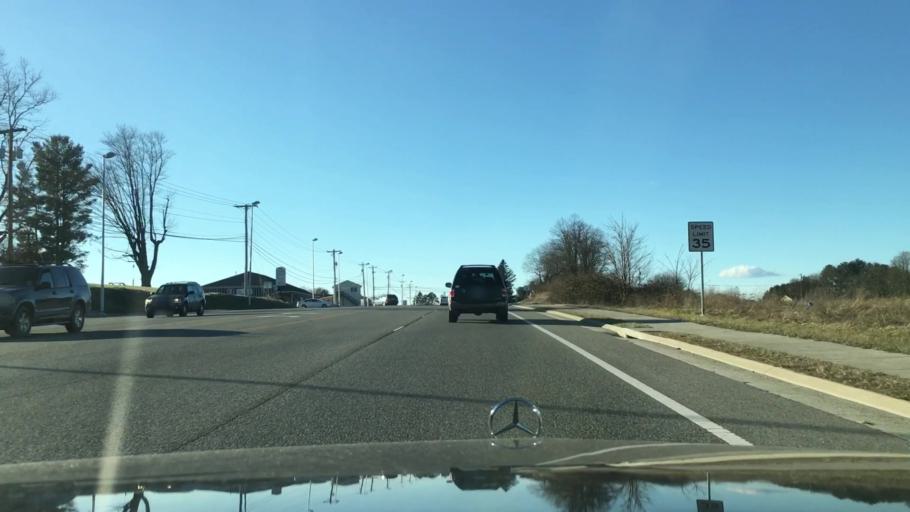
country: US
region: Virginia
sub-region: Montgomery County
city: Merrimac
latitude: 37.1626
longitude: -80.4335
